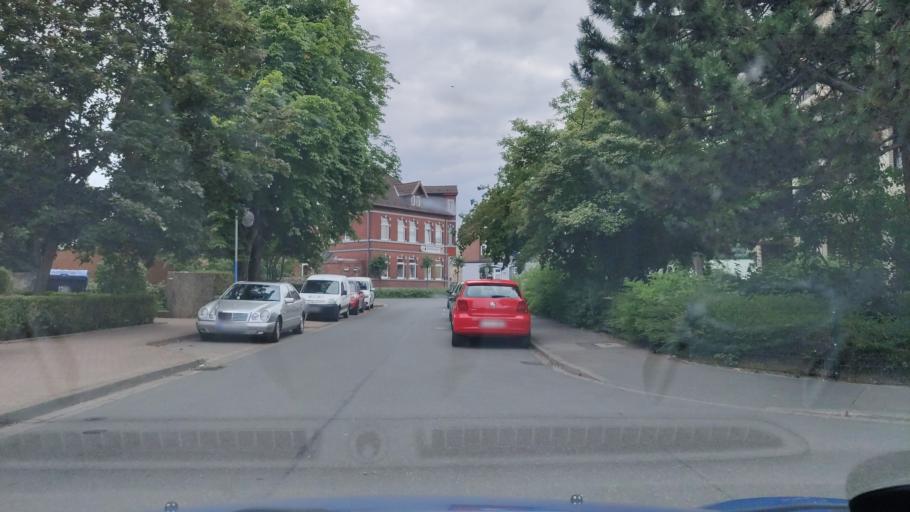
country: DE
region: Lower Saxony
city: Ronnenberg
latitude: 52.3417
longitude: 9.6638
